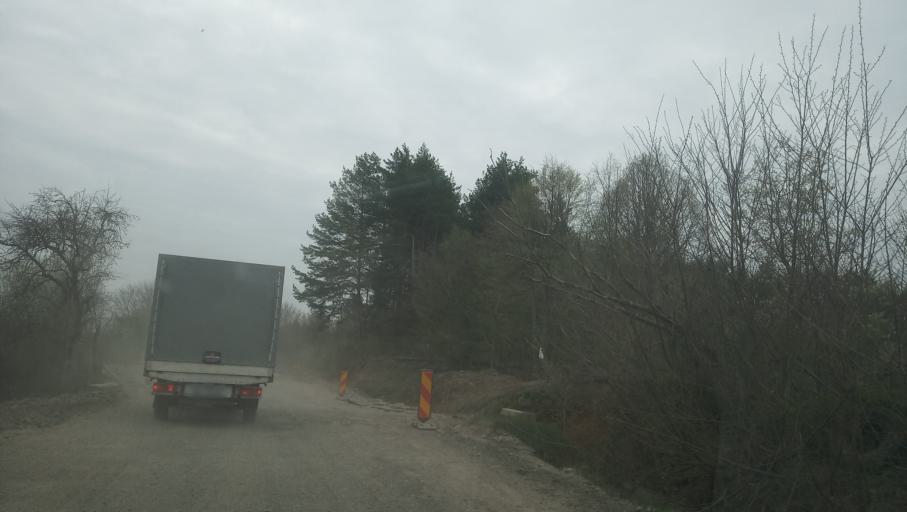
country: RO
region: Arad
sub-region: Comuna Varfurile
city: Varfurile
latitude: 46.3667
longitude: 22.5493
